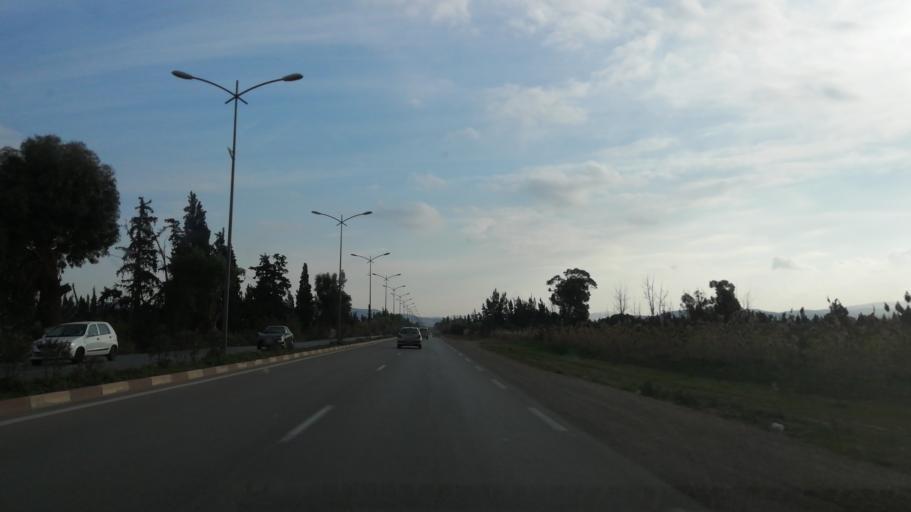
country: DZ
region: Mascara
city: Mascara
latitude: 35.6205
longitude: 0.0620
